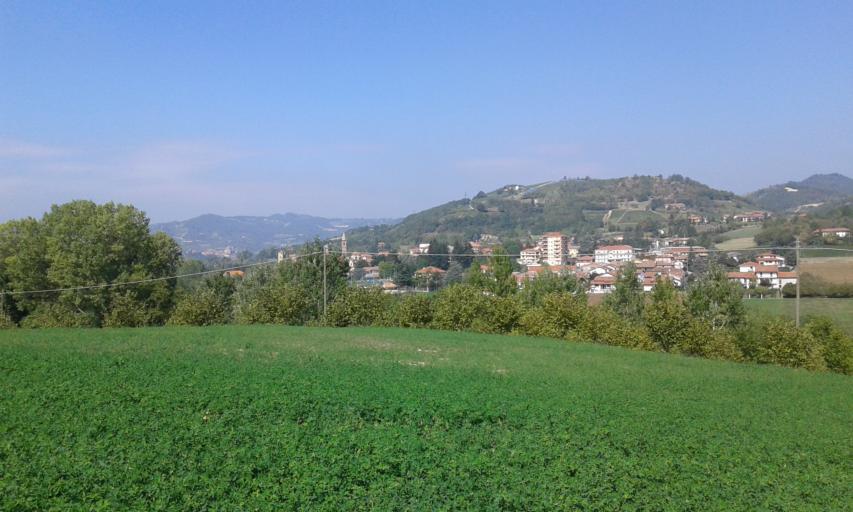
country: IT
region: Piedmont
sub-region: Provincia di Asti
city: Monastero Bormida
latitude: 44.6427
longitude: 8.3316
